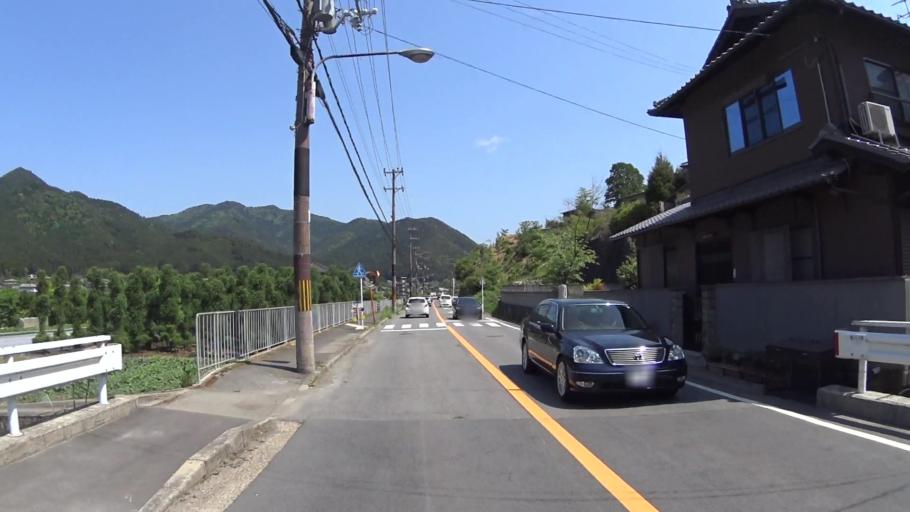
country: JP
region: Kyoto
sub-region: Kyoto-shi
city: Kamigyo-ku
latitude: 35.1076
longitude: 135.8239
